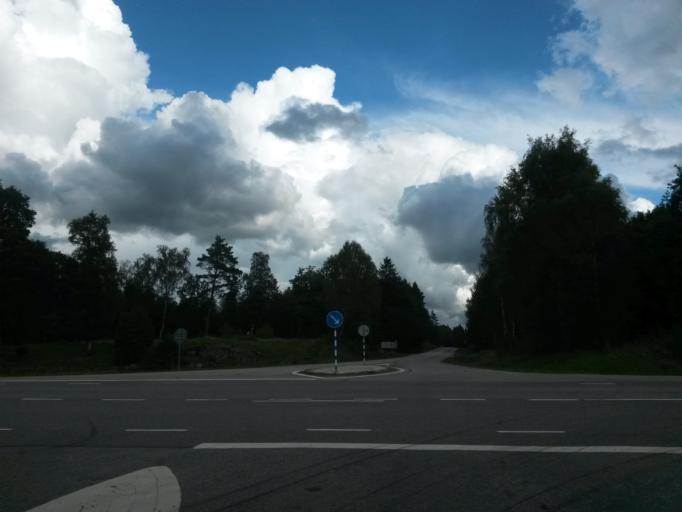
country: SE
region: Vaestra Goetaland
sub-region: Vargarda Kommun
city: Vargarda
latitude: 57.9903
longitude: 12.8123
